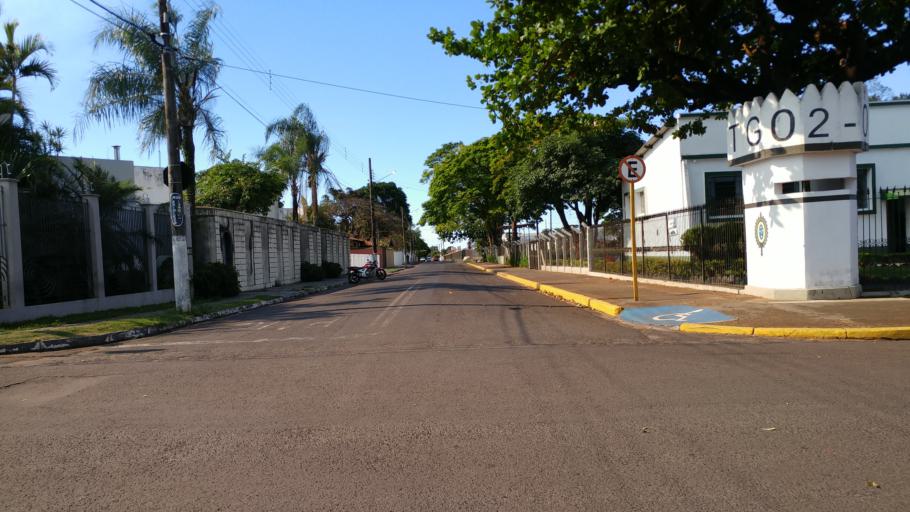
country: BR
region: Sao Paulo
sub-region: Paraguacu Paulista
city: Paraguacu Paulista
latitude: -22.4117
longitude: -50.5820
